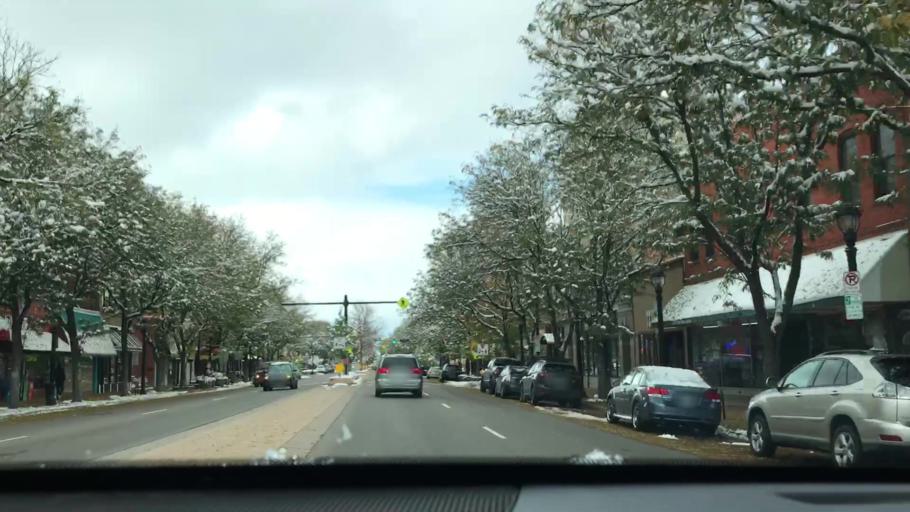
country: US
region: Colorado
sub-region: Boulder County
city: Longmont
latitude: 40.1660
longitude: -105.1025
